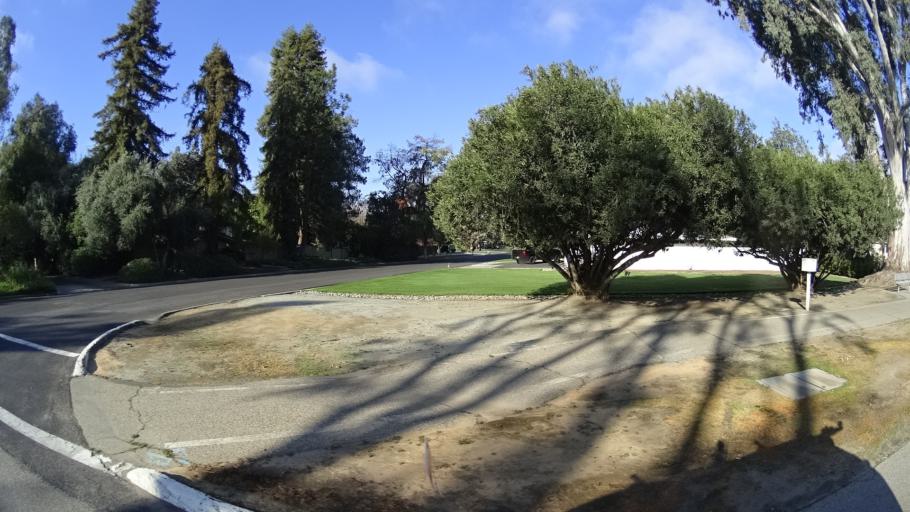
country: US
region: California
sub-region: Fresno County
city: Fresno
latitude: 36.8118
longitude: -119.8351
